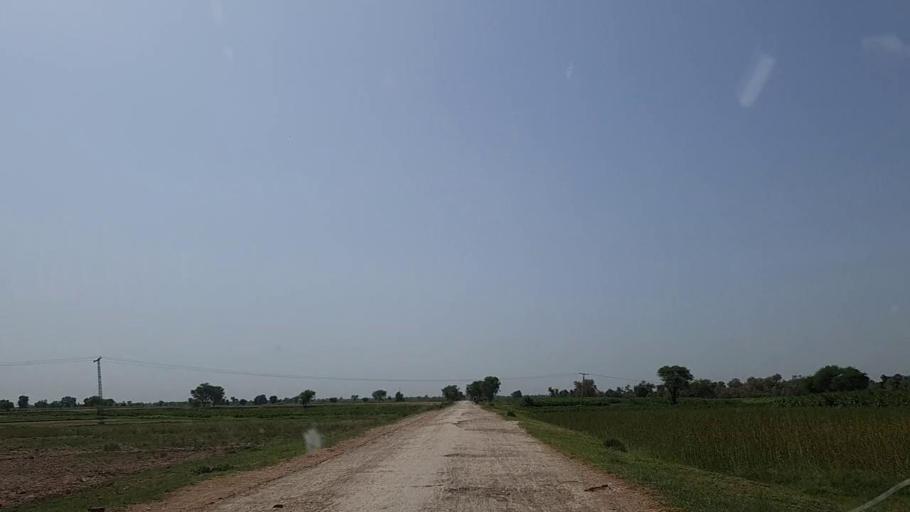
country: PK
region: Sindh
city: Naushahro Firoz
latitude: 26.8479
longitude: 68.0116
